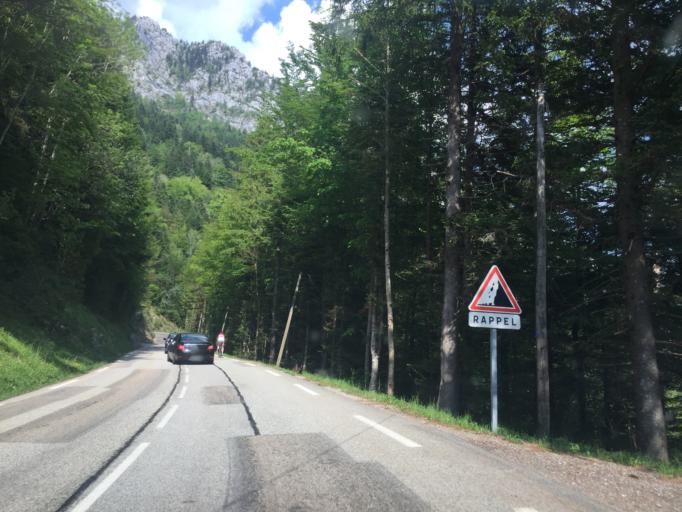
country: FR
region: Rhone-Alpes
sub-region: Departement de l'Isere
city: Saint-Laurent-du-Pont
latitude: 45.3480
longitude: 5.7881
